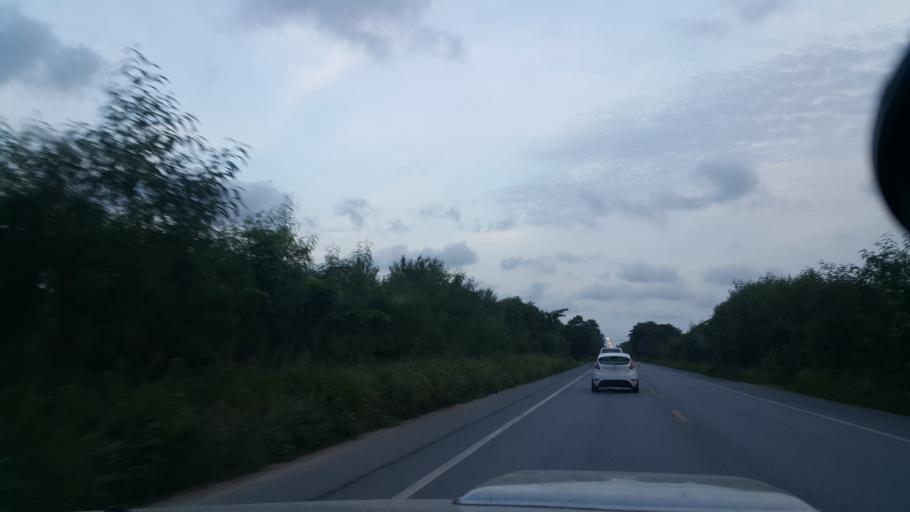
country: TH
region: Rayong
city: Ban Chang
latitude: 12.7205
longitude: 100.9904
